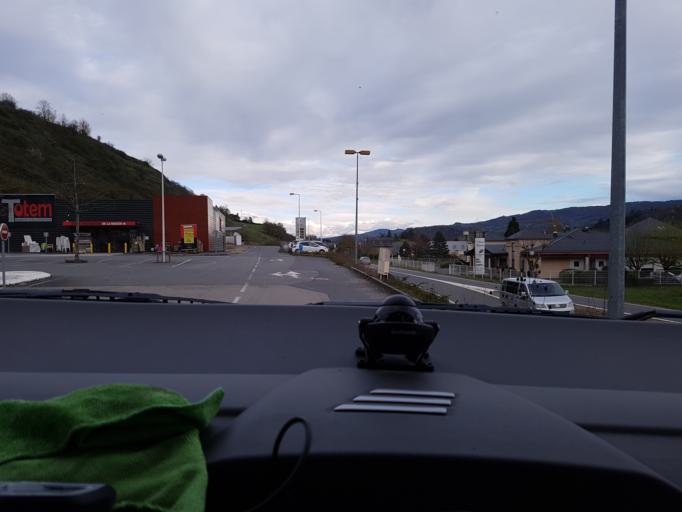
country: FR
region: Midi-Pyrenees
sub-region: Departement de l'Aveyron
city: Espalion
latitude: 44.5321
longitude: 2.7418
